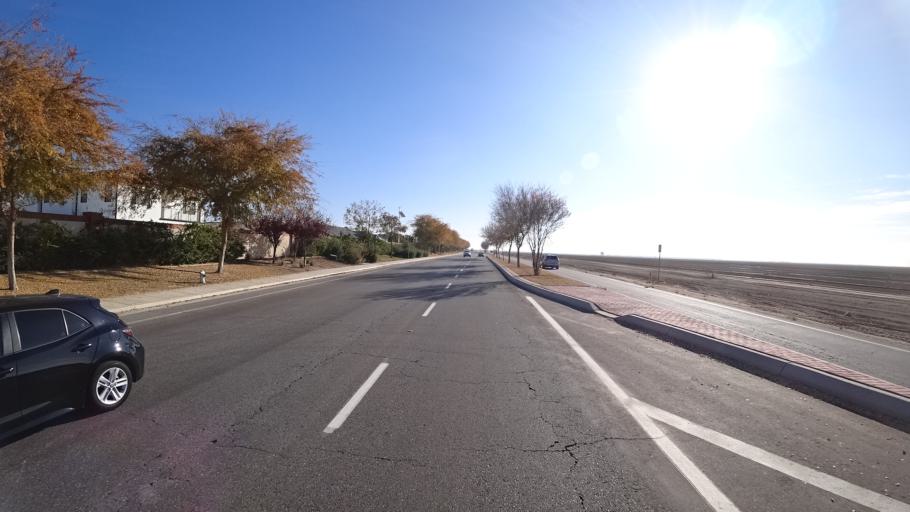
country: US
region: California
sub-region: Kern County
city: Rosedale
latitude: 35.3291
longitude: -119.1456
